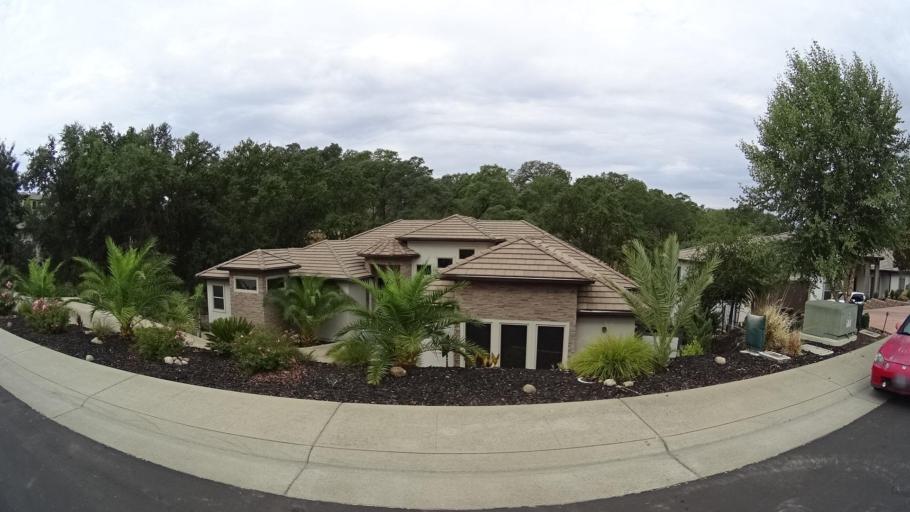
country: US
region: California
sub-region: Placer County
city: Rocklin
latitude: 38.7728
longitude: -121.2368
